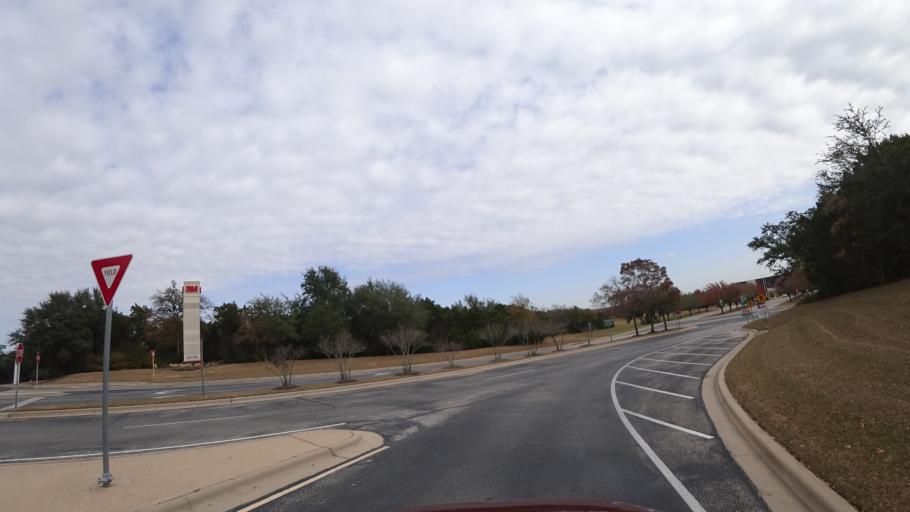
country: US
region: Texas
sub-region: Williamson County
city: Anderson Mill
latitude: 30.3956
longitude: -97.8446
